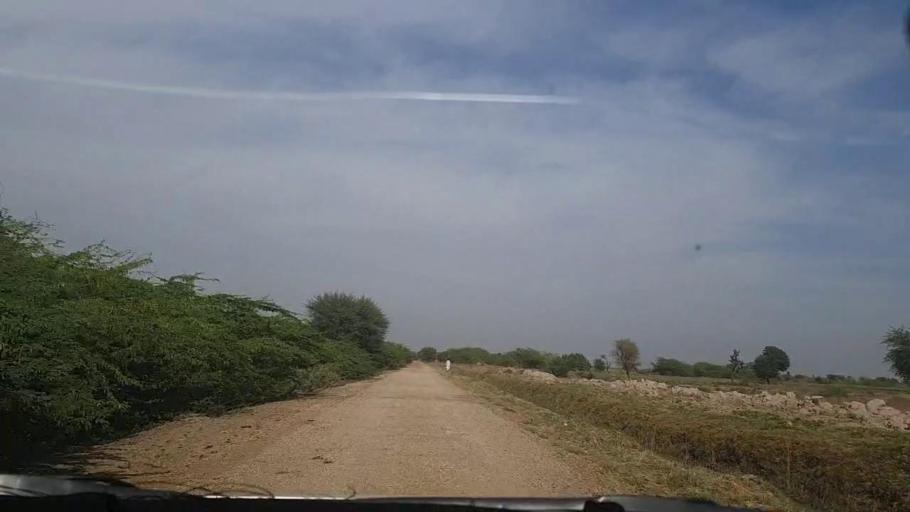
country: PK
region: Sindh
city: Pithoro
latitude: 25.5463
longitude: 69.3621
